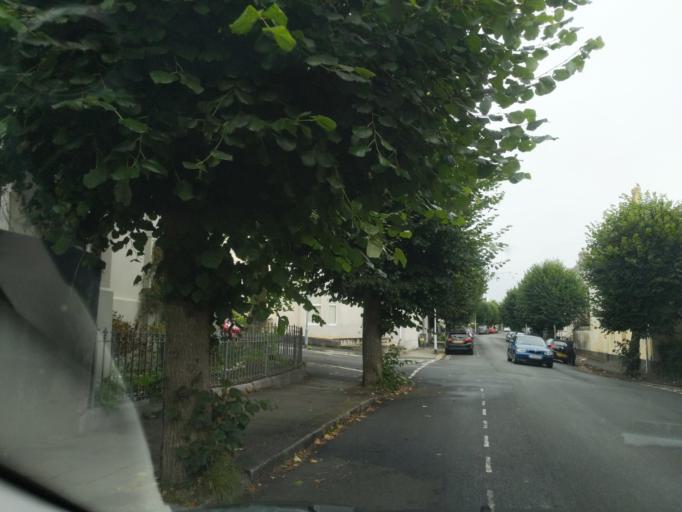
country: GB
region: England
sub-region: Plymouth
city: Plymouth
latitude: 50.3743
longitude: -4.1275
